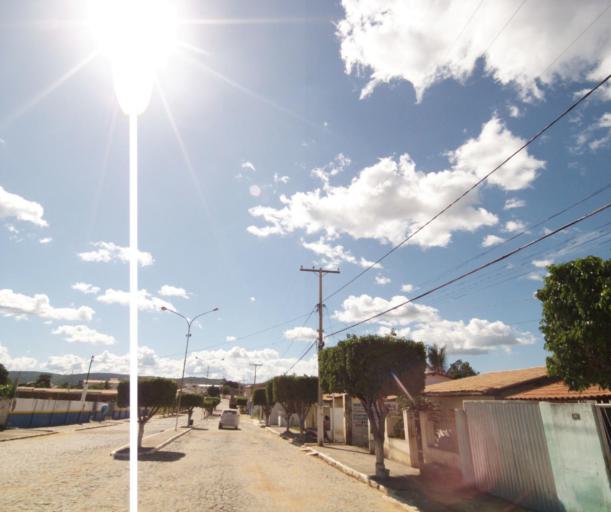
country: BR
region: Bahia
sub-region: Pocoes
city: Pocoes
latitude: -14.2415
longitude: -40.7688
